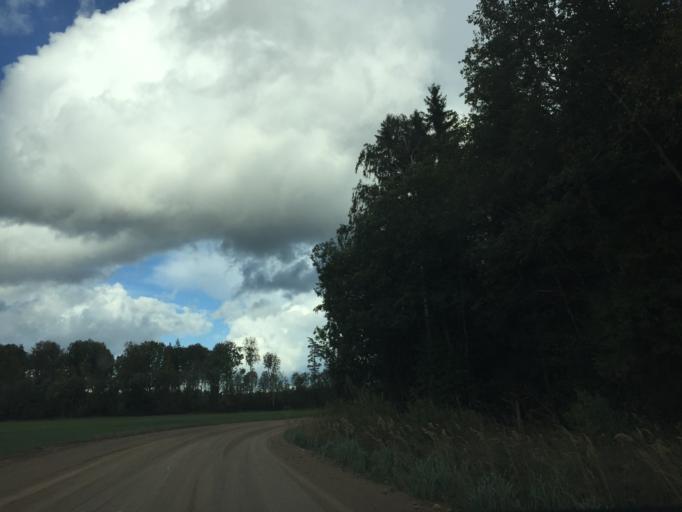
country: LV
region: Malpils
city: Malpils
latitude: 57.0565
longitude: 25.1312
